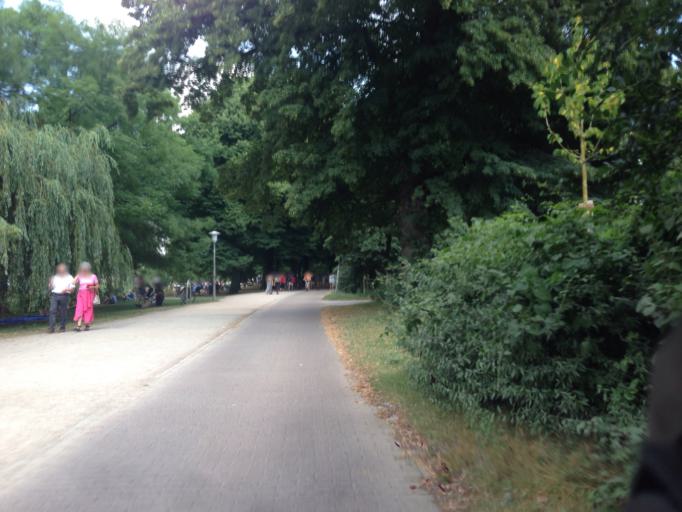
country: DE
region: Hamburg
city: St. Georg
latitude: 53.5598
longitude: 10.0100
